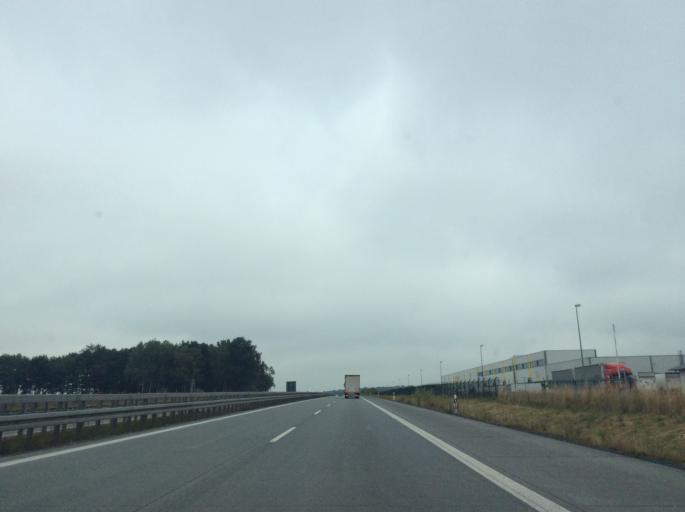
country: DE
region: Saxony
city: Thiendorf
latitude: 51.2979
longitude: 13.7325
